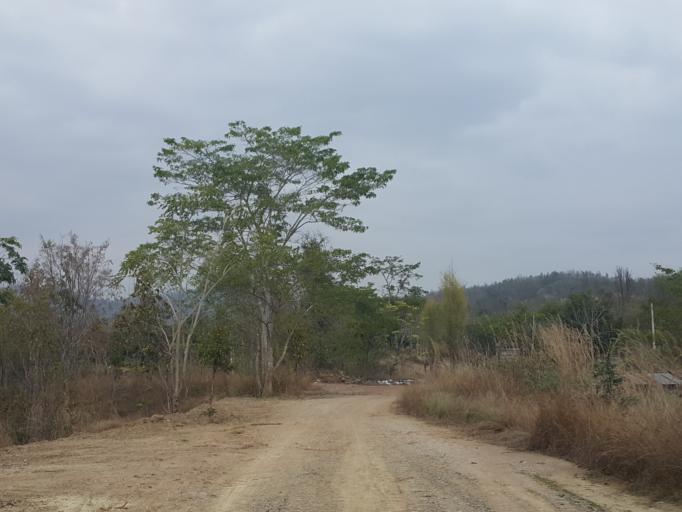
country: TH
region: Chiang Mai
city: Hang Dong
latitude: 18.7063
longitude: 98.8734
